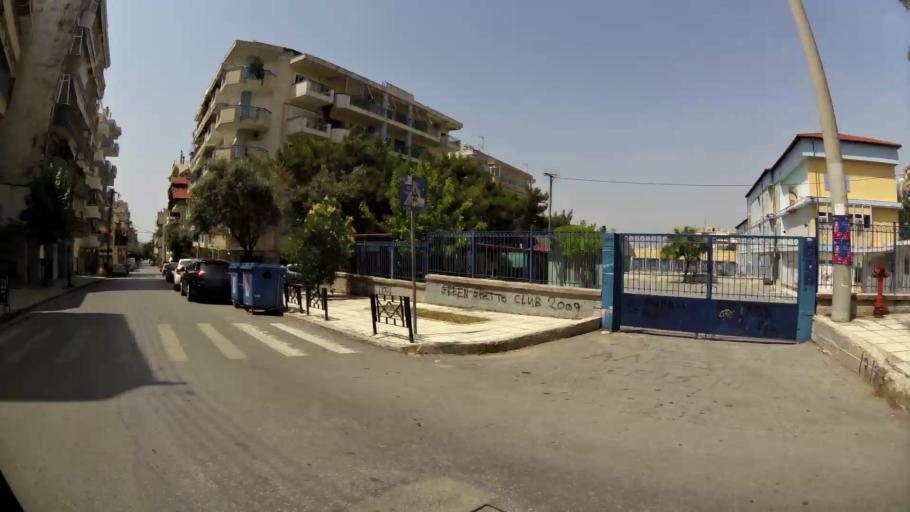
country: GR
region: Central Macedonia
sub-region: Nomos Thessalonikis
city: Evosmos
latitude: 40.6728
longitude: 22.9049
